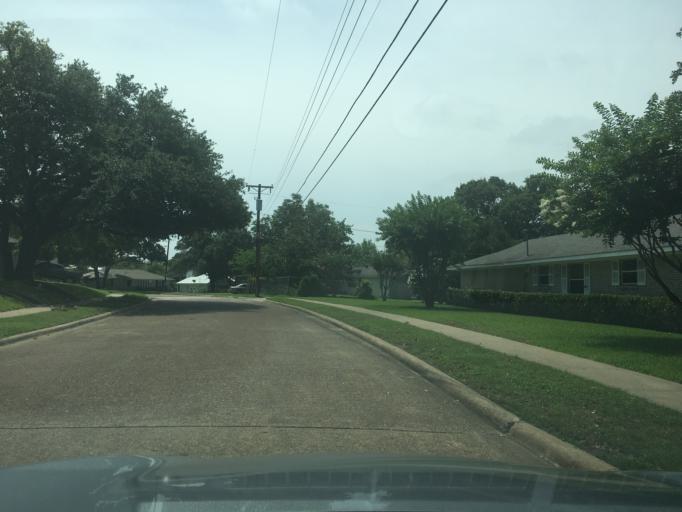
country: US
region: Texas
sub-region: Dallas County
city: Richardson
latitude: 32.9436
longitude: -96.7541
